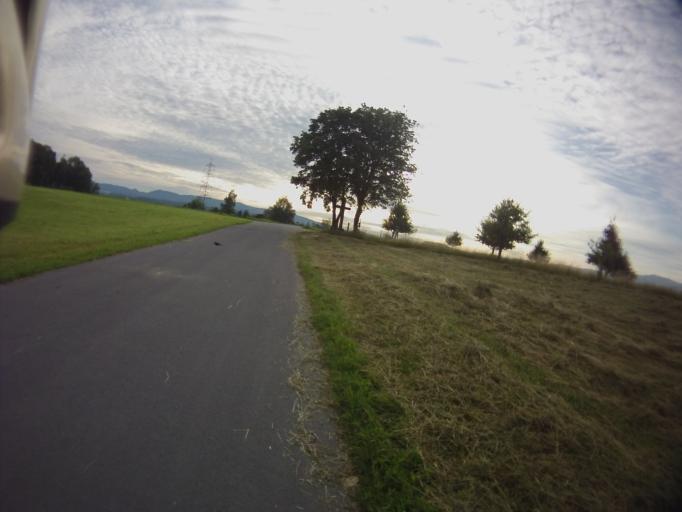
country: CH
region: Zug
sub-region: Zug
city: Cham
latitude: 47.1878
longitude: 8.4629
